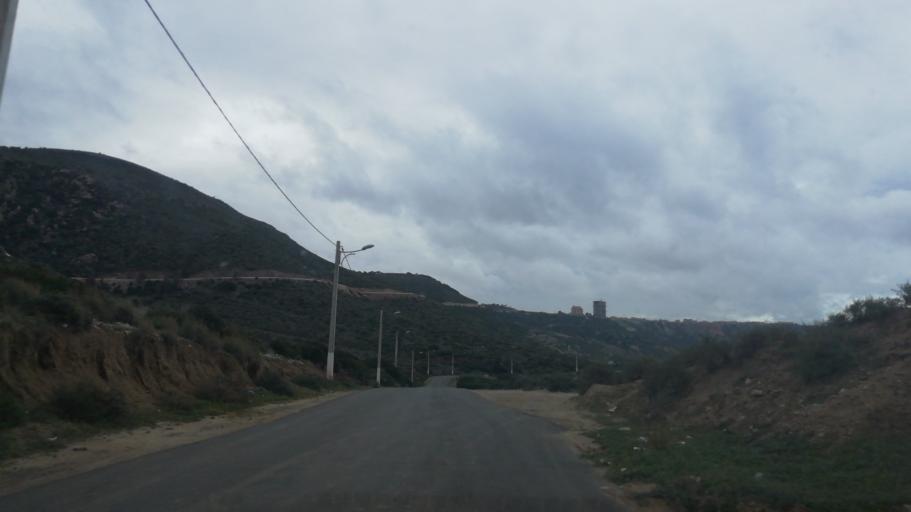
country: DZ
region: Oran
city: Bir el Djir
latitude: 35.7734
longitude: -0.5171
